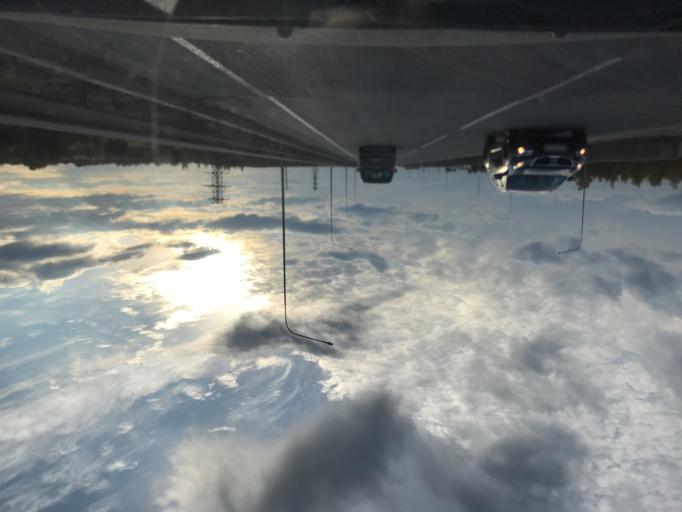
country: RU
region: Kaluga
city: Kurovskoye
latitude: 54.5334
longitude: 35.9951
